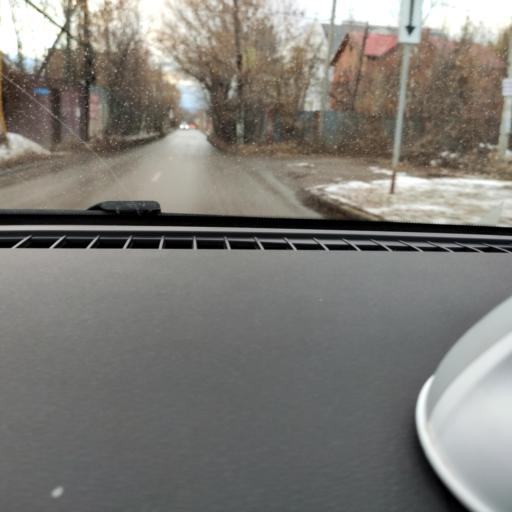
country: RU
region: Samara
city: Samara
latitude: 53.2350
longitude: 50.1771
